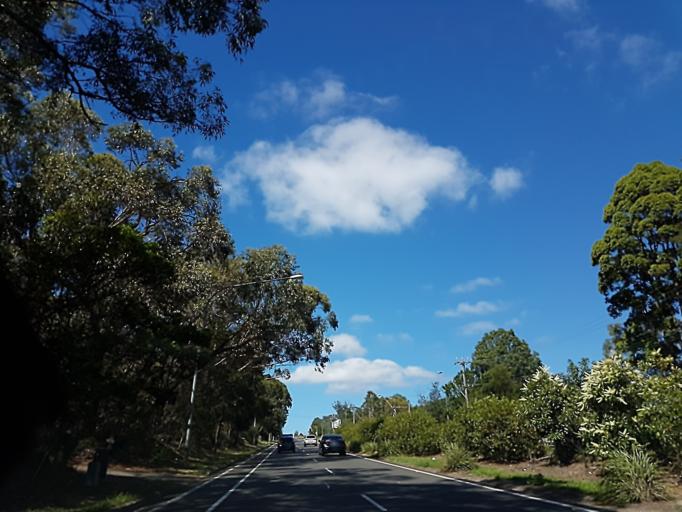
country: AU
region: New South Wales
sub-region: Warringah
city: Davidson
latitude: -33.7142
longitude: 151.2173
